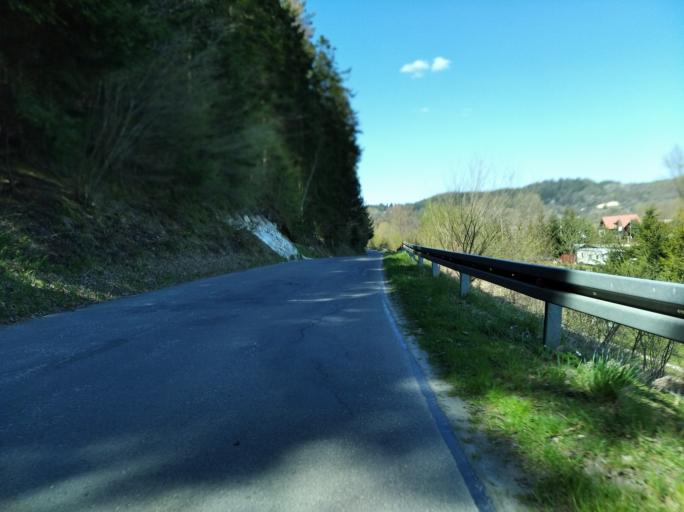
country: PL
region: Subcarpathian Voivodeship
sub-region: Powiat brzozowski
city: Dydnia
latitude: 49.6933
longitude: 22.2038
